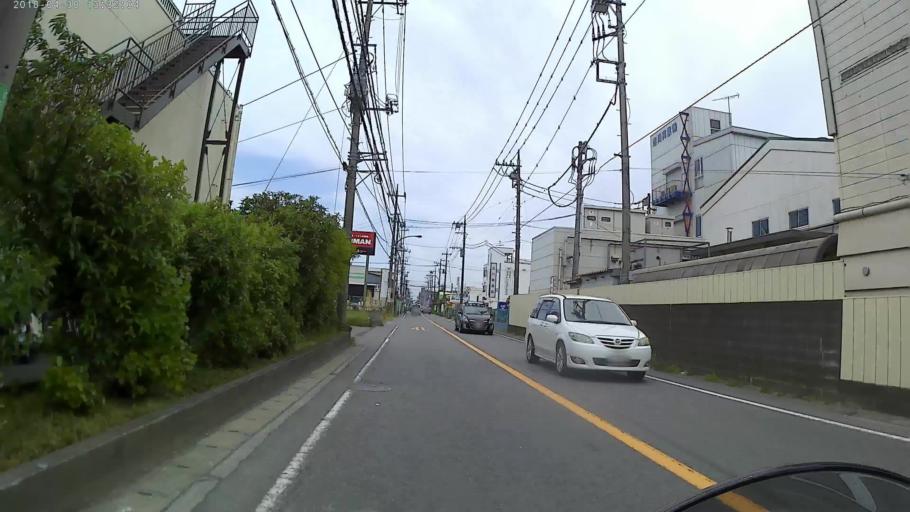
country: JP
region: Tokyo
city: Hachioji
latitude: 35.5904
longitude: 139.3306
